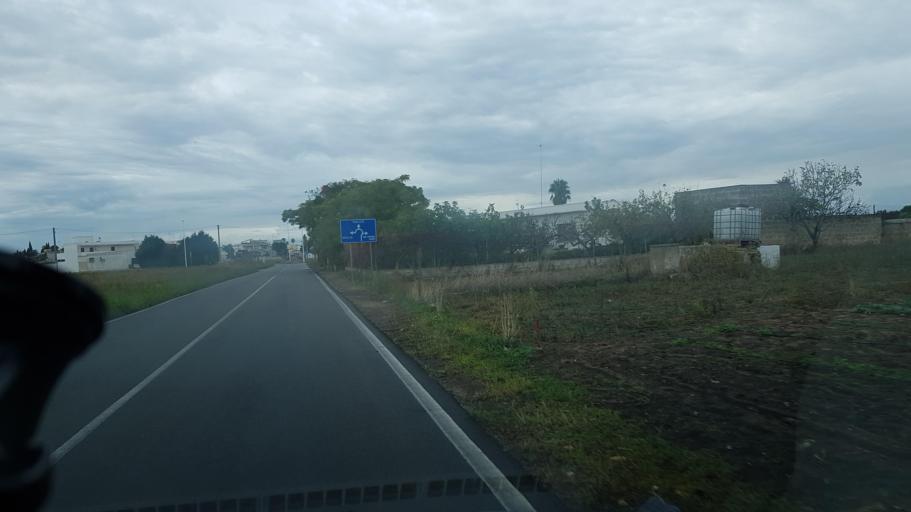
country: IT
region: Apulia
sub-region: Provincia di Lecce
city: Salice Salentino
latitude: 40.3798
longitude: 17.9722
